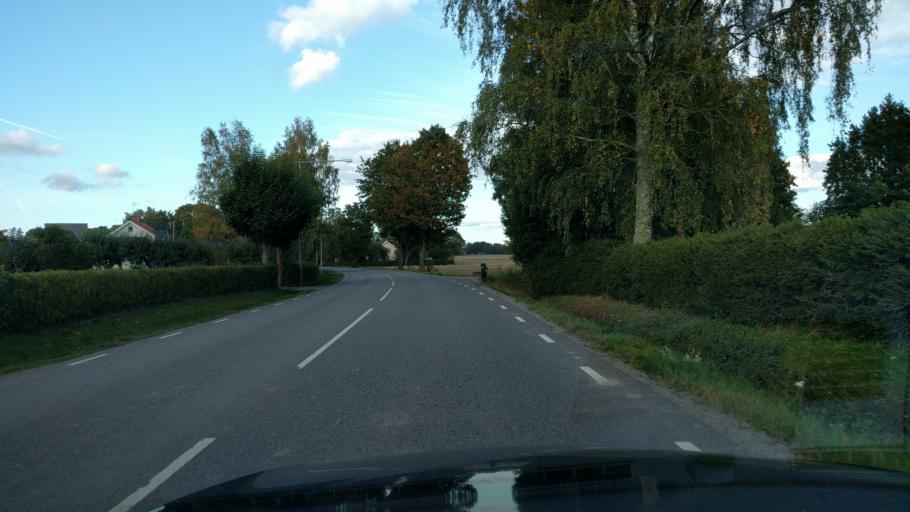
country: SE
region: Uppsala
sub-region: Tierps Kommun
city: Orbyhus
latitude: 60.1584
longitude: 17.5977
